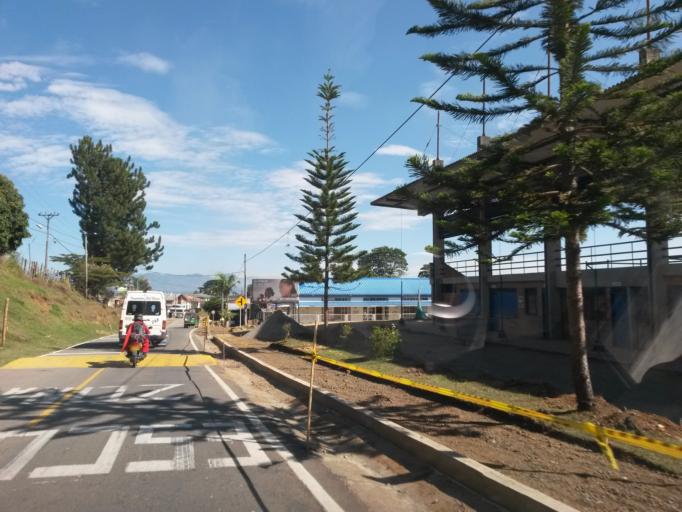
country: CO
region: Cauca
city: Morales
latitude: 2.7504
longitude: -76.6268
